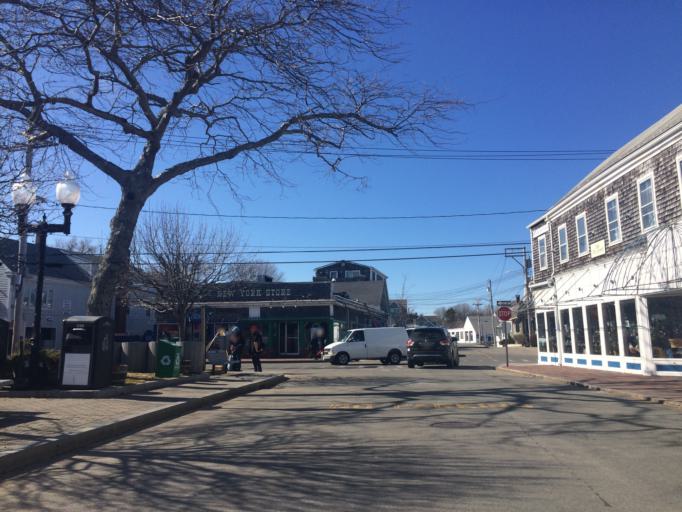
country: US
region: Massachusetts
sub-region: Barnstable County
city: Provincetown
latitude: 42.0517
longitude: -70.1854
